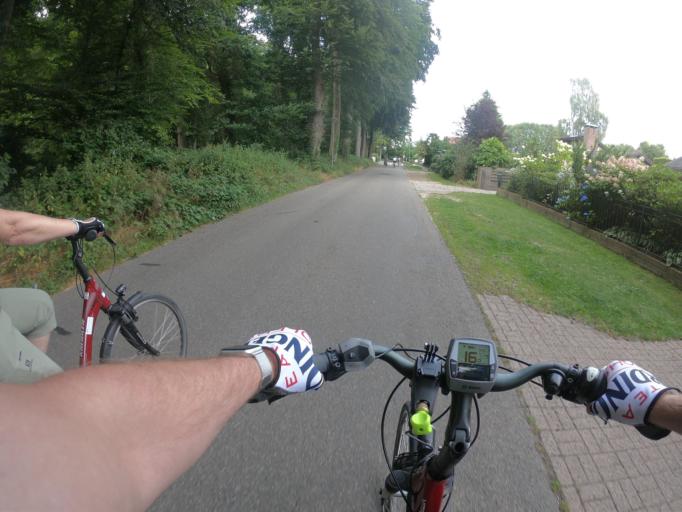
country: NL
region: Gelderland
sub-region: Gemeente Groesbeek
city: Groesbeek
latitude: 51.7731
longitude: 5.9280
